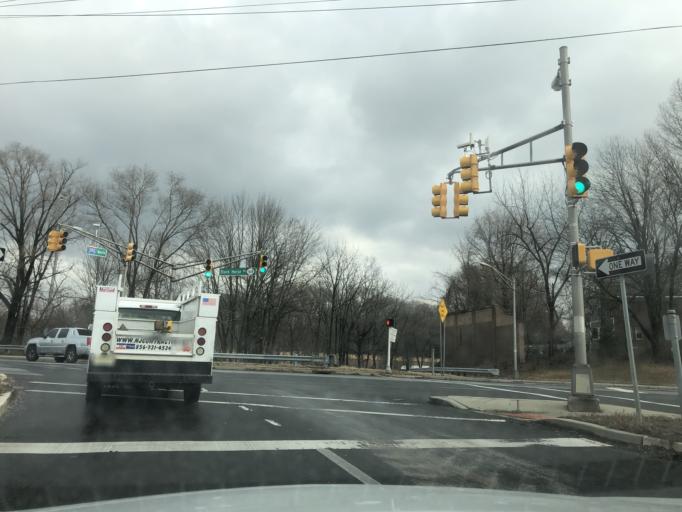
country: US
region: New Jersey
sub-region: Camden County
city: Mount Ephraim
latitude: 39.8717
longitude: -75.0821
